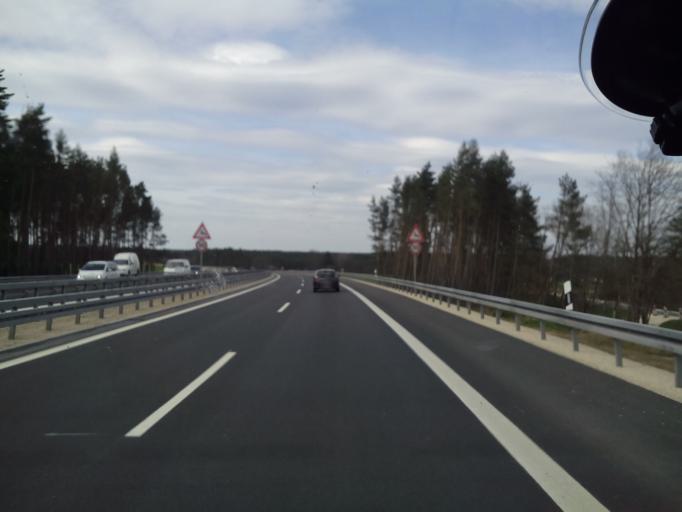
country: DE
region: Bavaria
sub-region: Regierungsbezirk Mittelfranken
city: Roth
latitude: 49.2015
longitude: 11.0759
